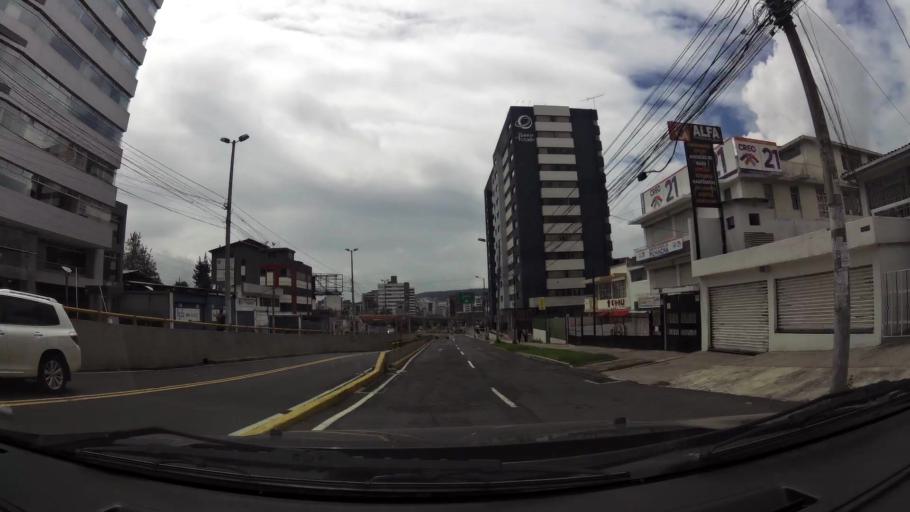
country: EC
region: Pichincha
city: Quito
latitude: -0.1845
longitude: -78.4922
